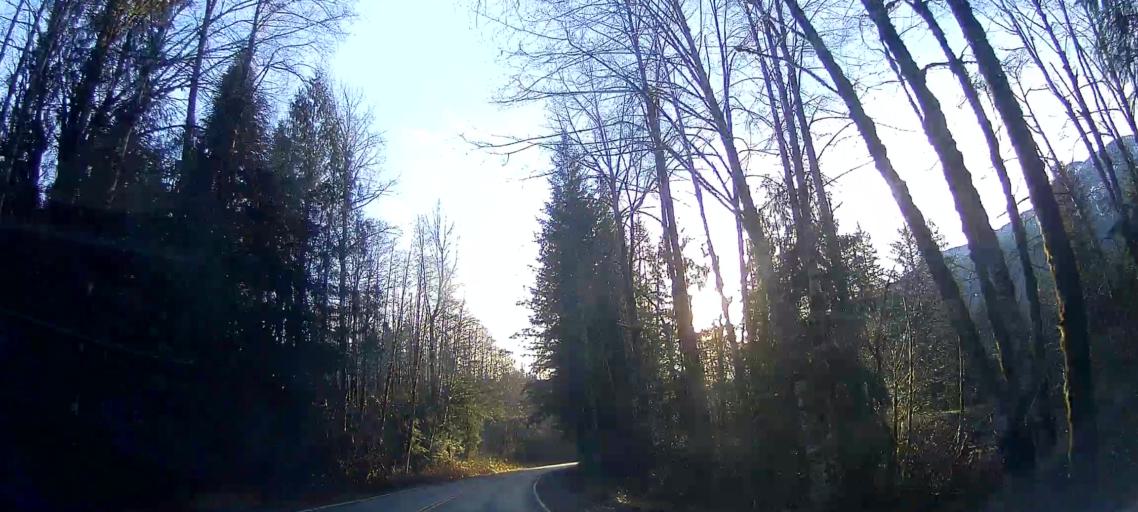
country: US
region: Washington
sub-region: Snohomish County
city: Darrington
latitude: 48.6081
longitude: -121.7561
